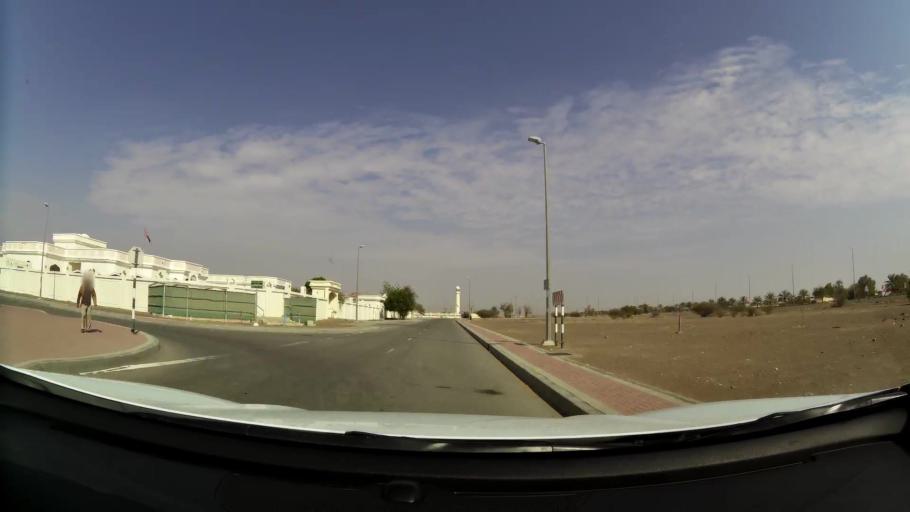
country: AE
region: Abu Dhabi
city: Al Ain
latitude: 24.0951
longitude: 55.9247
